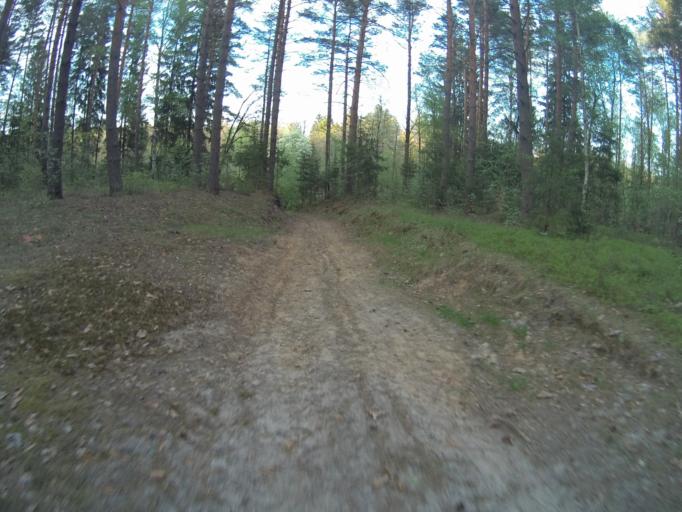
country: RU
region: Vladimir
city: Kommunar
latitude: 56.0669
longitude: 40.4748
